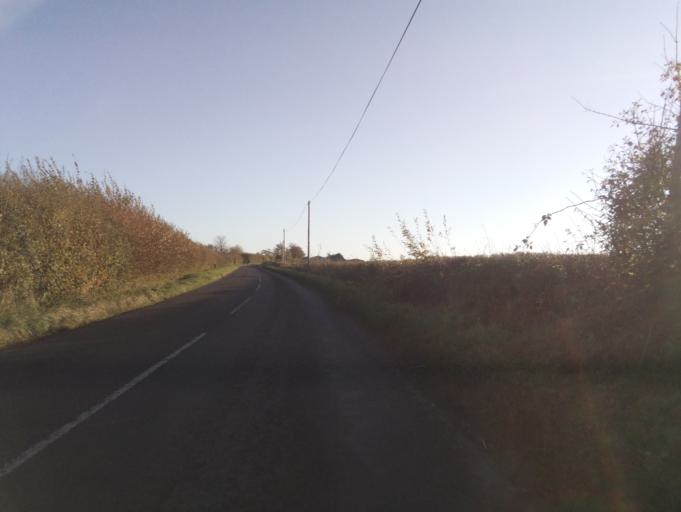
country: GB
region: England
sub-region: Somerset
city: Milborne Port
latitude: 50.9810
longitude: -2.4636
